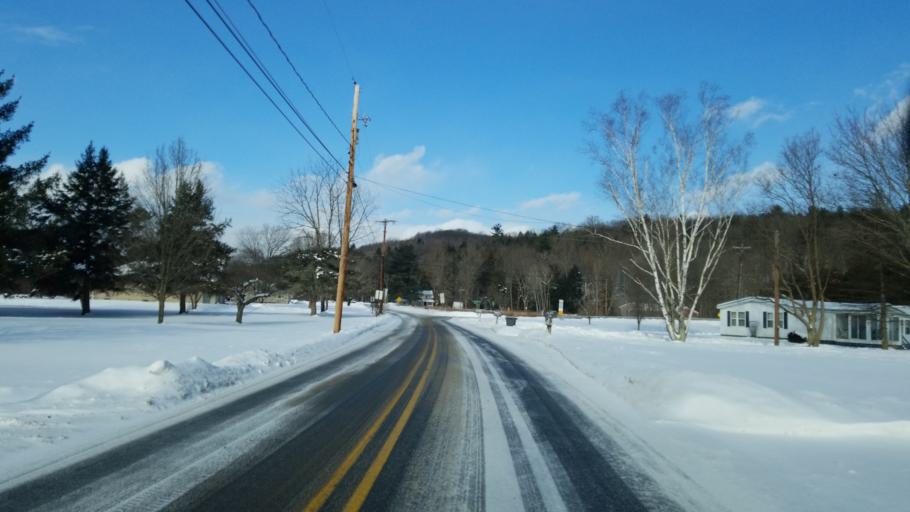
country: US
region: Pennsylvania
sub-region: Clearfield County
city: Hyde
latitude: 41.0124
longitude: -78.4712
